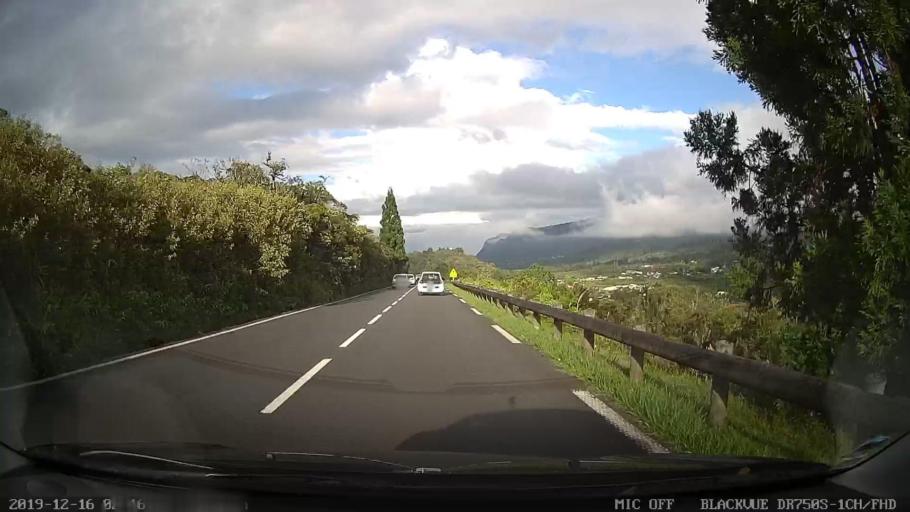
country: RE
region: Reunion
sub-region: Reunion
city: Cilaos
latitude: -21.1562
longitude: 55.6004
